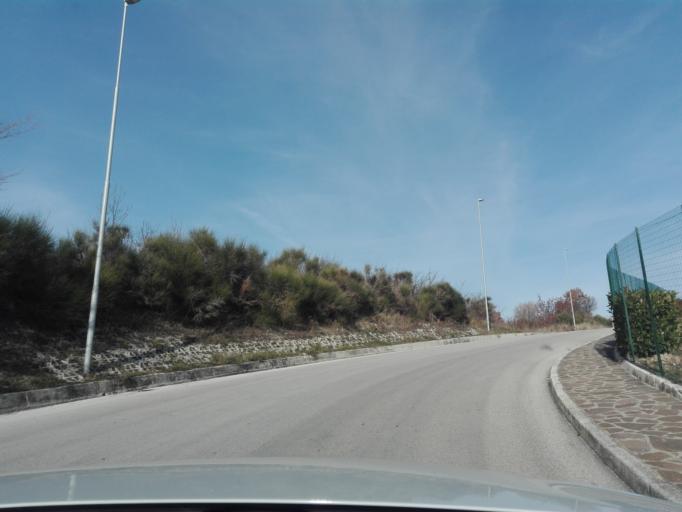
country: IT
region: Molise
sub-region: Provincia di Isernia
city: Agnone
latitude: 41.8159
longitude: 14.3698
